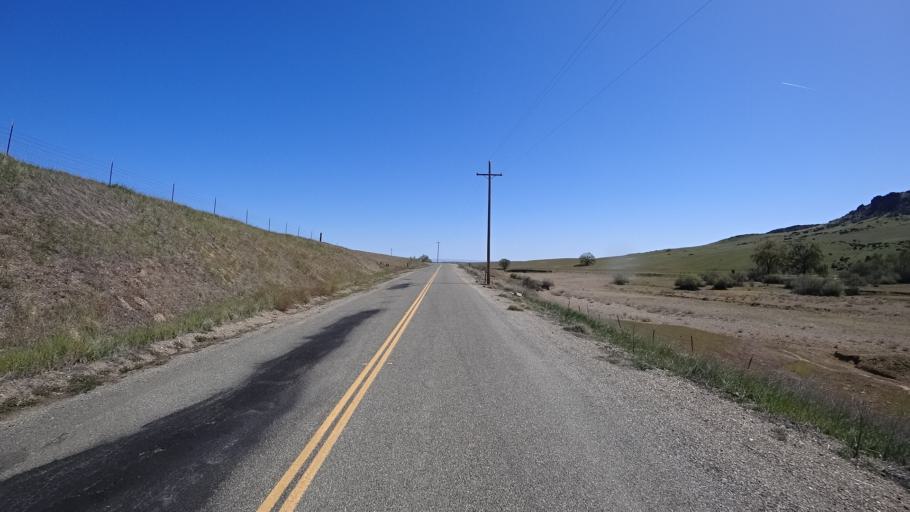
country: US
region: California
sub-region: Glenn County
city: Orland
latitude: 39.7628
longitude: -122.3386
